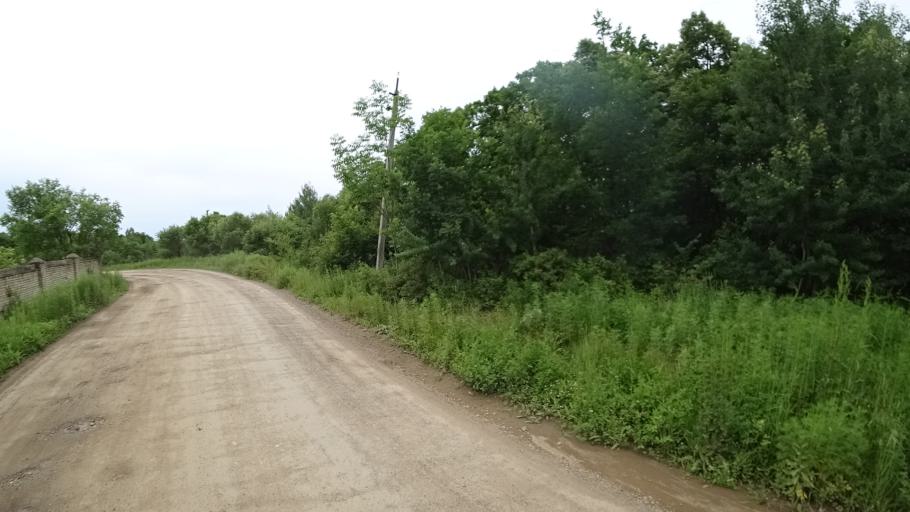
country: RU
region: Primorskiy
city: Arsen'yev
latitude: 44.1976
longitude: 133.3080
